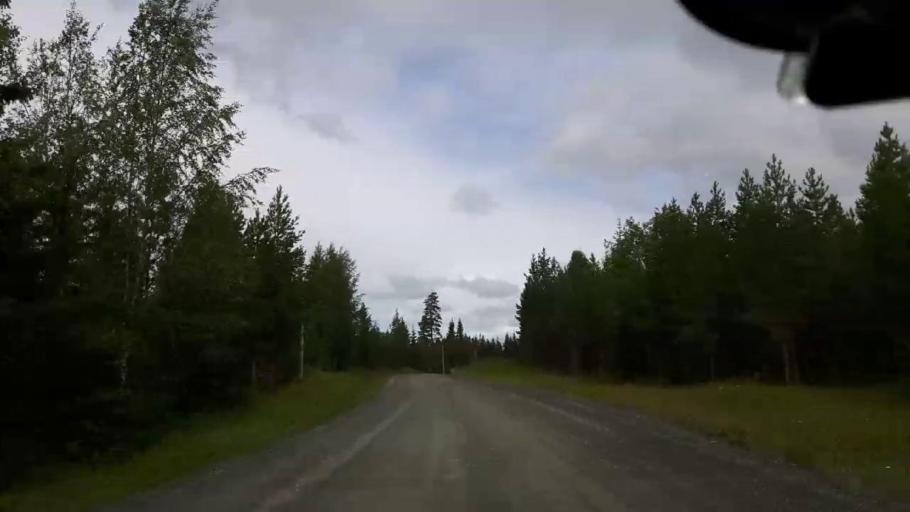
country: SE
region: Jaemtland
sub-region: Krokoms Kommun
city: Valla
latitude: 63.4178
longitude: 14.0805
